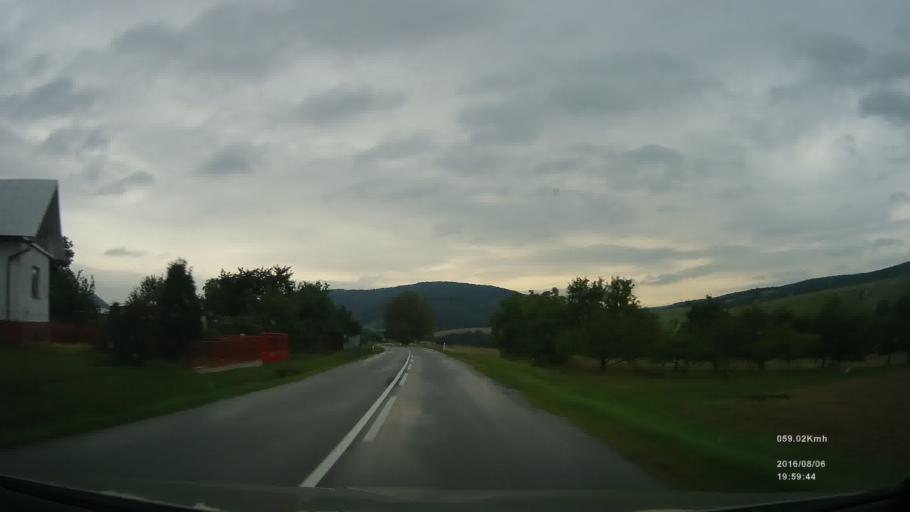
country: SK
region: Presovsky
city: Svidnik
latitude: 49.2597
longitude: 21.5801
